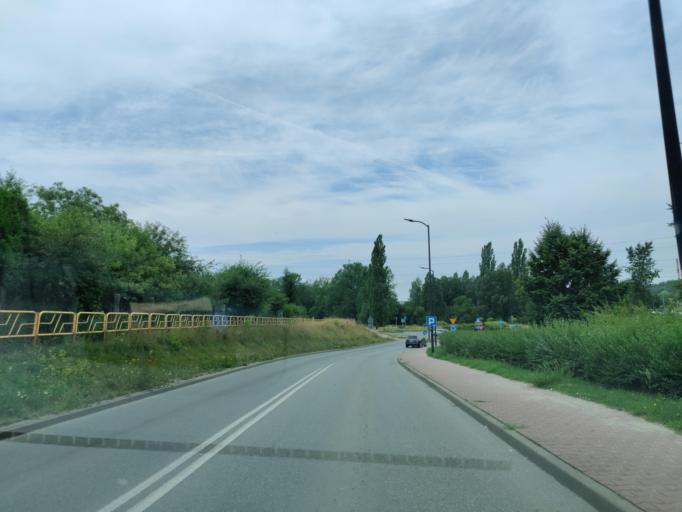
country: PL
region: Silesian Voivodeship
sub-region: Powiat bedzinski
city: Bedzin
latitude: 50.2888
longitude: 19.1605
